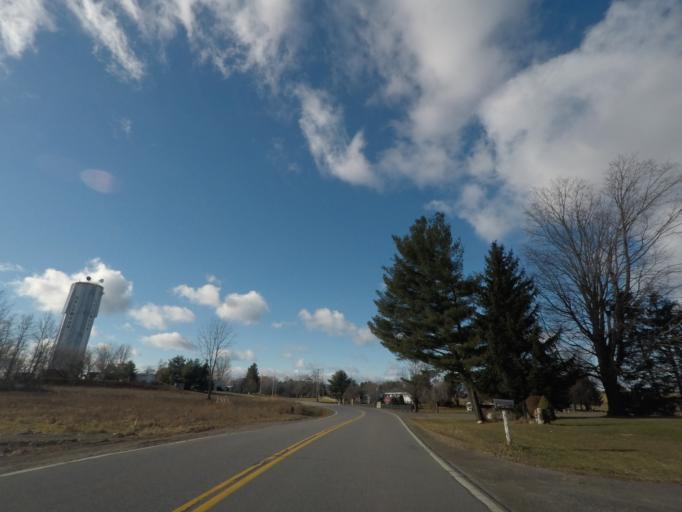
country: US
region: New York
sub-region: Saratoga County
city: Waterford
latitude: 42.8315
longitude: -73.7040
